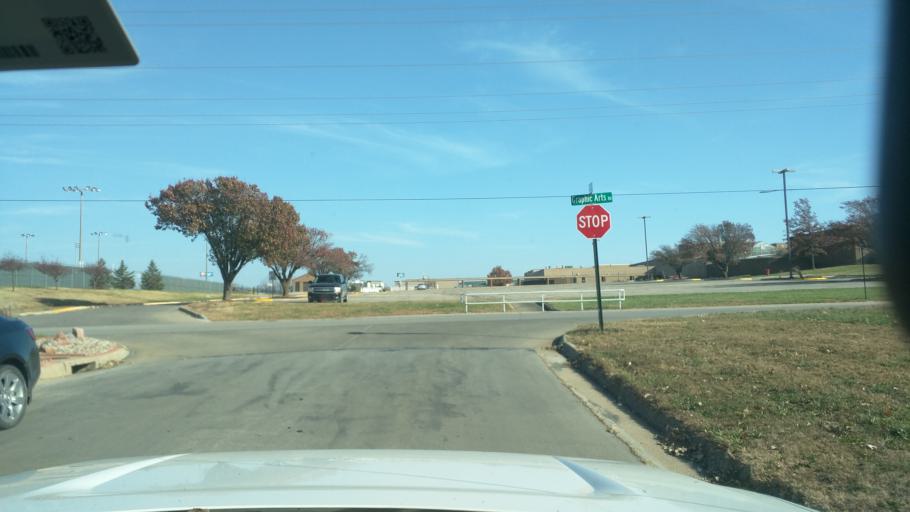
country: US
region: Kansas
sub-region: Lyon County
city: Emporia
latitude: 38.4218
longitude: -96.2265
